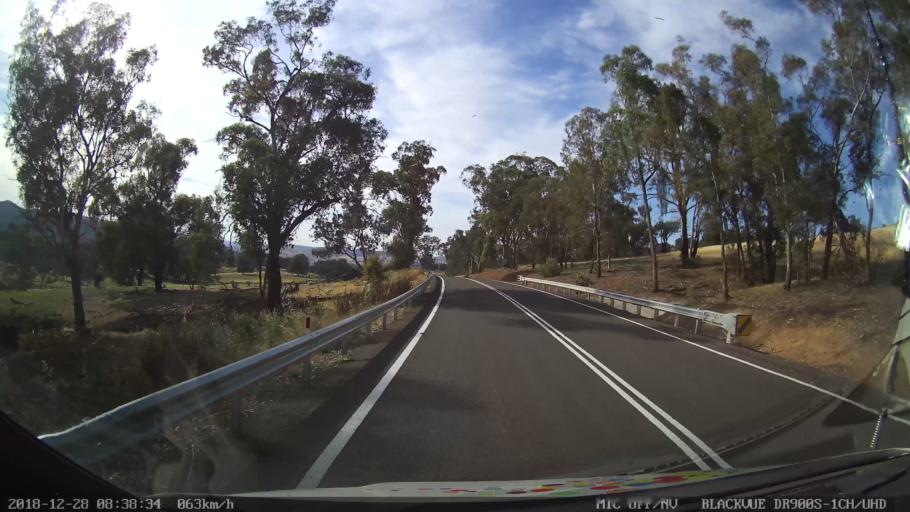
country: AU
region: New South Wales
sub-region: Blayney
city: Blayney
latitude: -34.0049
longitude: 149.3156
